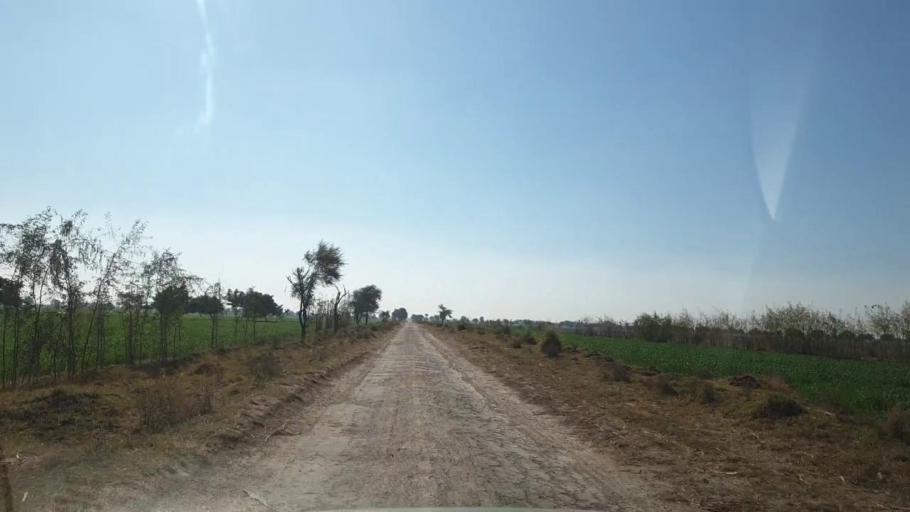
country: PK
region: Sindh
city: Jhol
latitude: 25.8221
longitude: 69.0359
